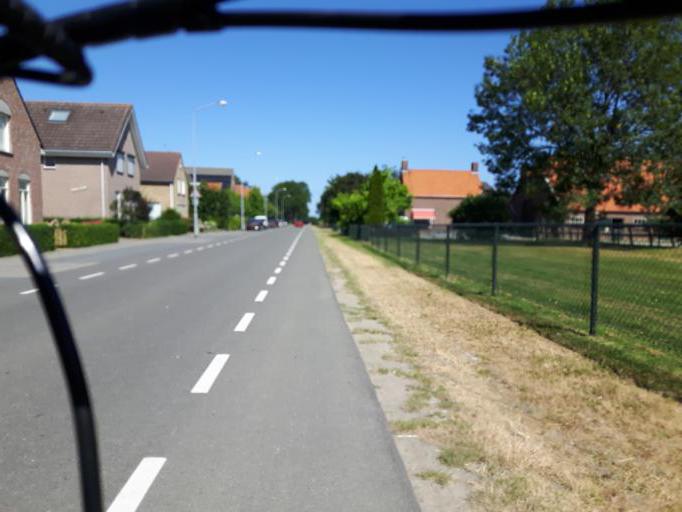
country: NL
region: North Brabant
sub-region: Gemeente Moerdijk
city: Klundert
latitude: 51.6694
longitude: 4.5325
